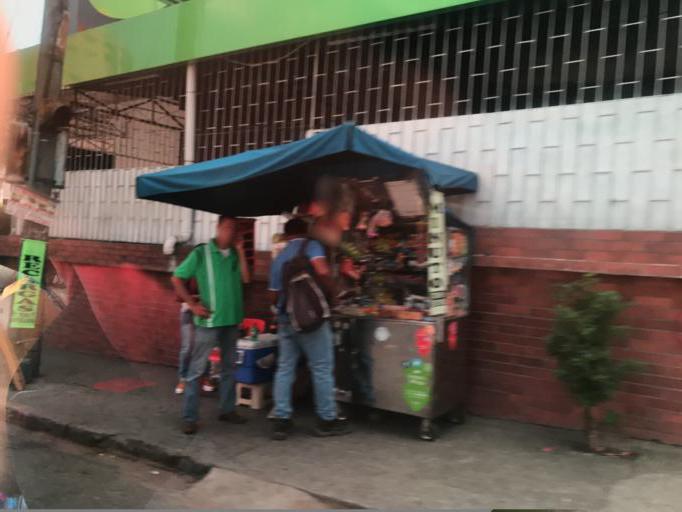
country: CO
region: Valle del Cauca
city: Cali
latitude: 3.4537
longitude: -76.5503
